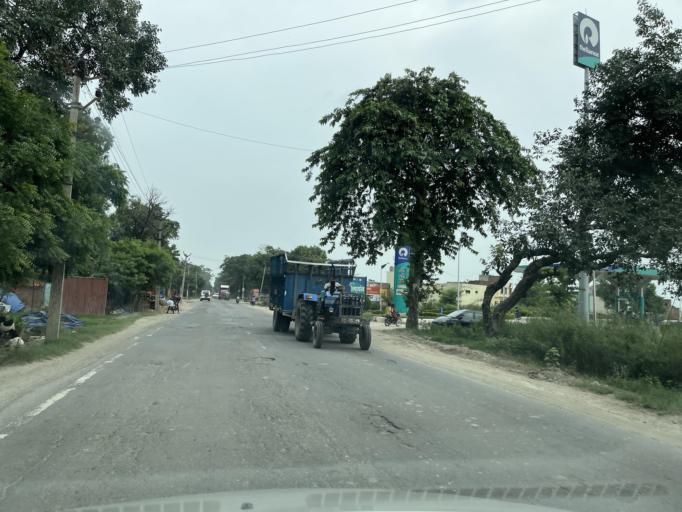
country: IN
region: Uttar Pradesh
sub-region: Rampur
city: Bilaspur
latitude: 29.0308
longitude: 79.2628
